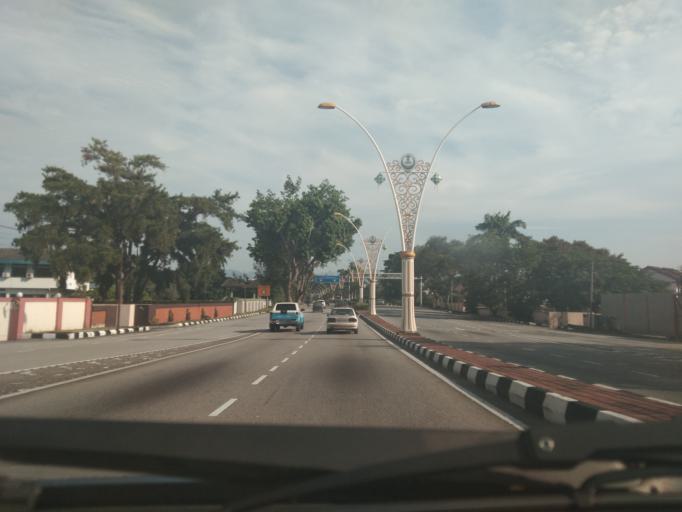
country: MY
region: Perak
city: Ipoh
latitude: 4.5826
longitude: 101.1022
